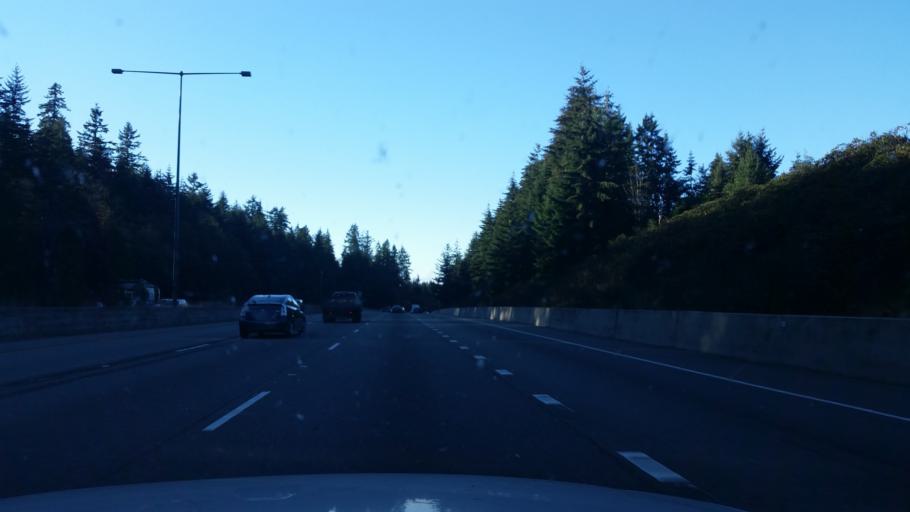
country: US
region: Washington
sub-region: Snohomish County
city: Martha Lake
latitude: 47.8225
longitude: -122.2477
